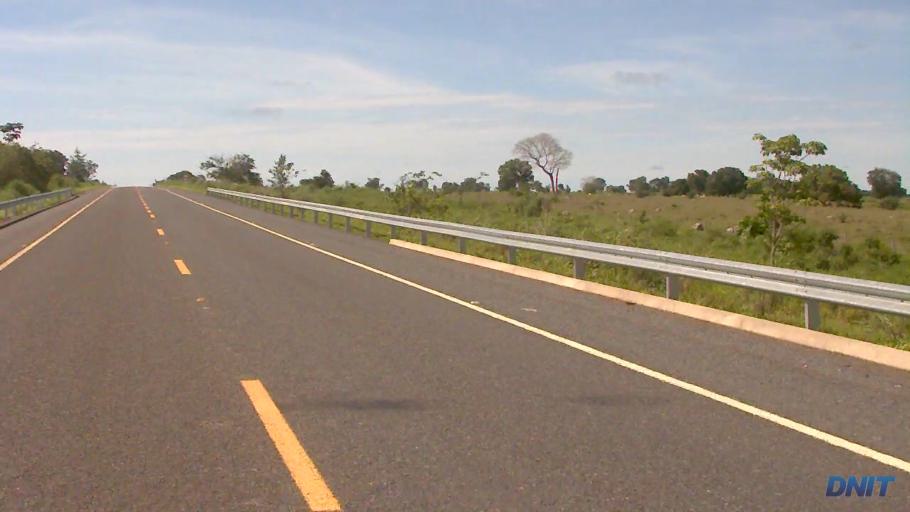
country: BR
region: Goias
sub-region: Sao Miguel Do Araguaia
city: Sao Miguel do Araguaia
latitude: -13.4533
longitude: -50.1199
